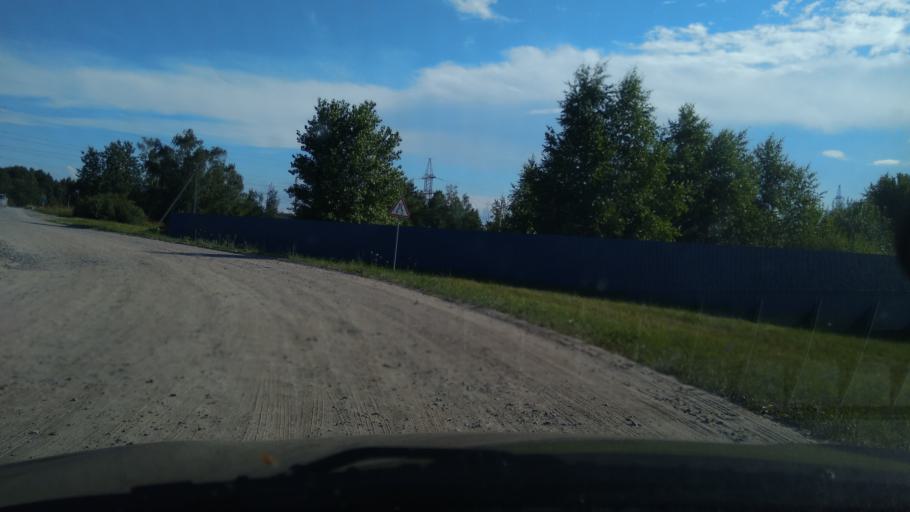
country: BY
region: Brest
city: Byelaazyorsk
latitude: 52.4566
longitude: 25.1866
